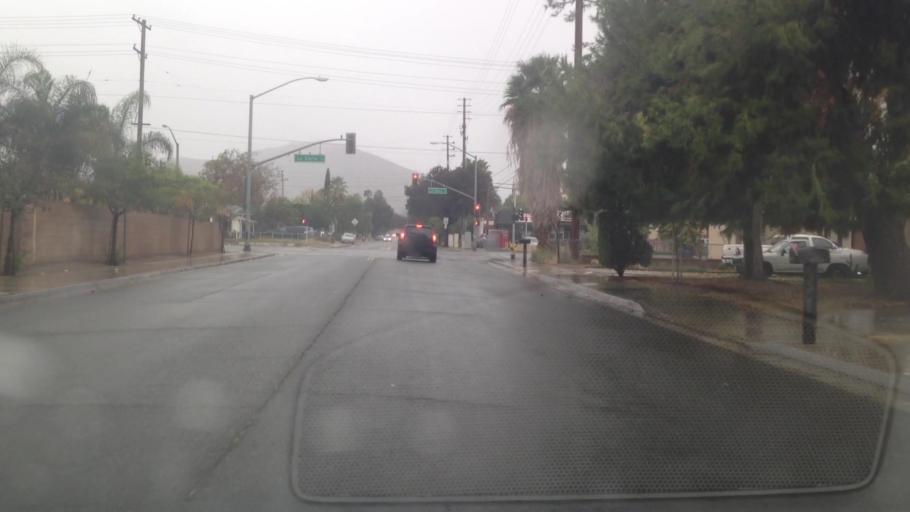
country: US
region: California
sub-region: Riverside County
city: Pedley
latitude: 33.9236
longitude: -117.4905
